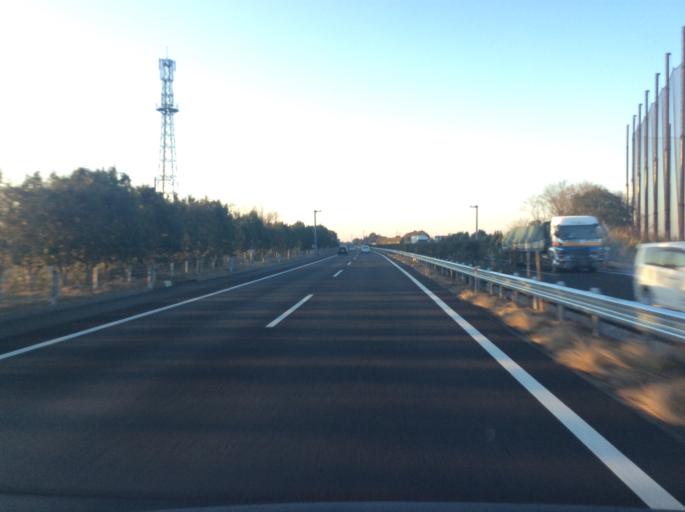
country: JP
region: Ibaraki
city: Mito-shi
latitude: 36.3907
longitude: 140.3873
